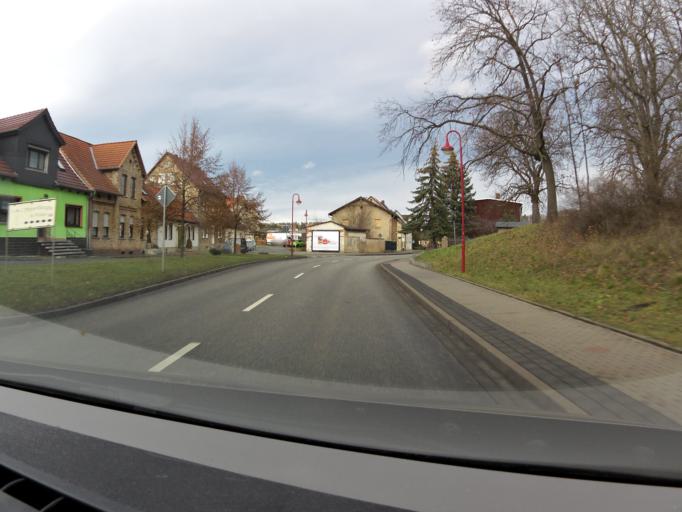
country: DE
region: Saxony-Anhalt
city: Mansfeld
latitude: 51.6021
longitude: 11.4626
